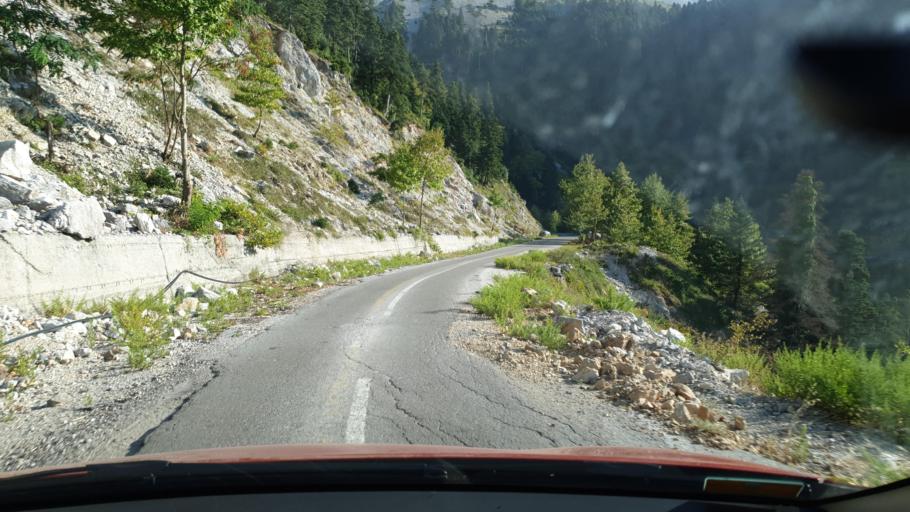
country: GR
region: Central Greece
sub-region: Nomos Evvoias
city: Yimnon
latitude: 38.5960
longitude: 23.9064
